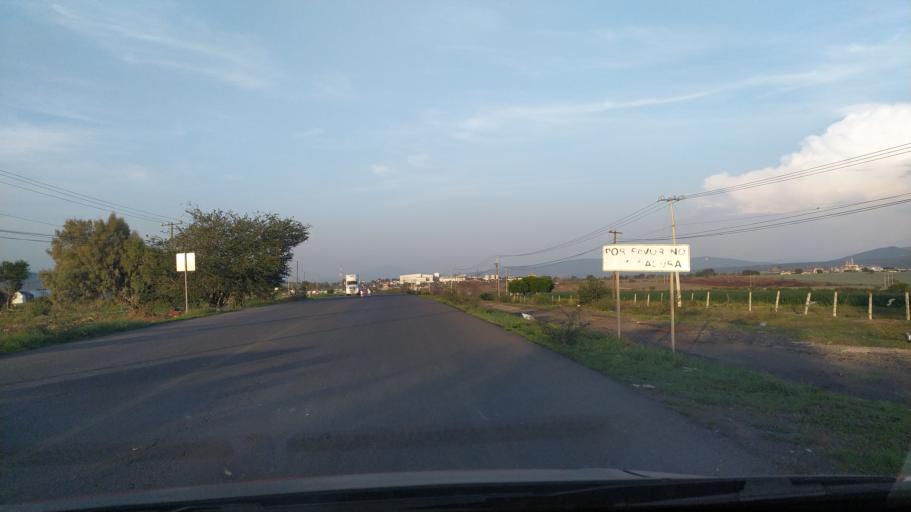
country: MX
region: Michoacan
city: Vistahermosa de Negrete
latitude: 20.2664
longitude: -102.4627
